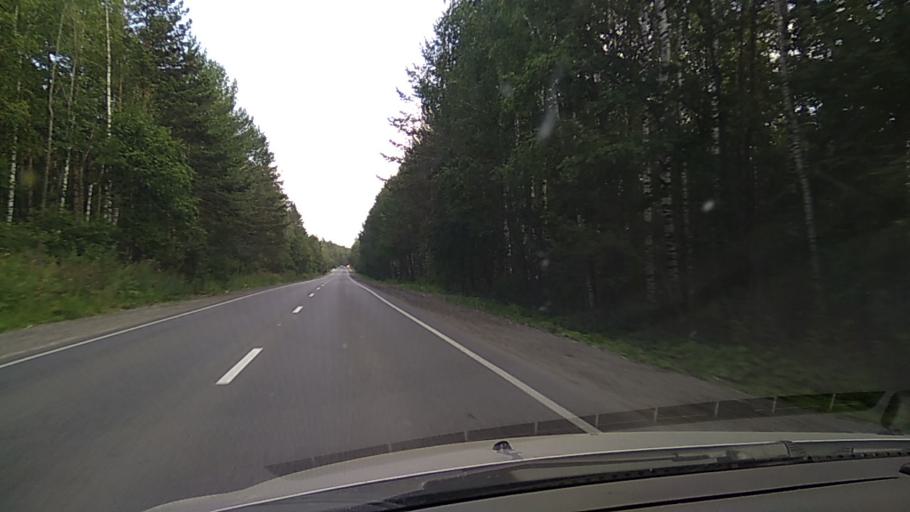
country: RU
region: Chelyabinsk
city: Syrostan
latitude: 55.1236
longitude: 59.7802
